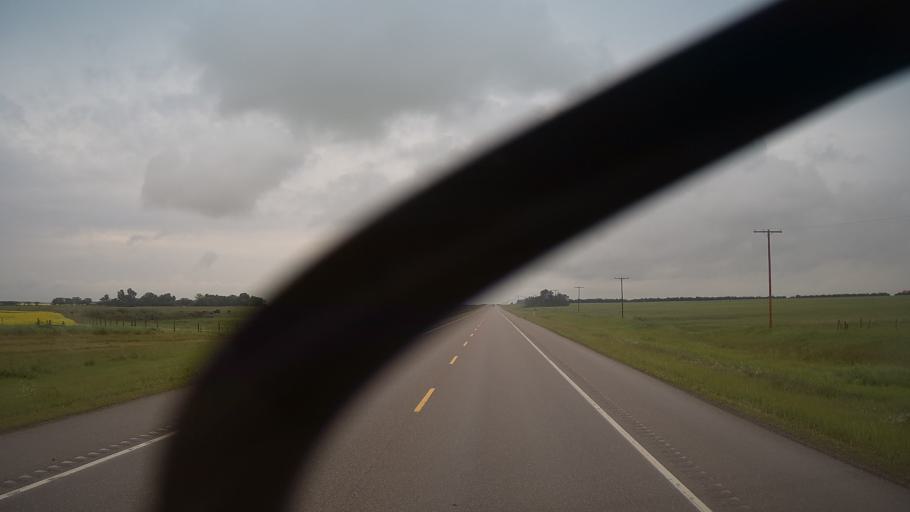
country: CA
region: Saskatchewan
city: Unity
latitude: 52.4348
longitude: -108.9409
